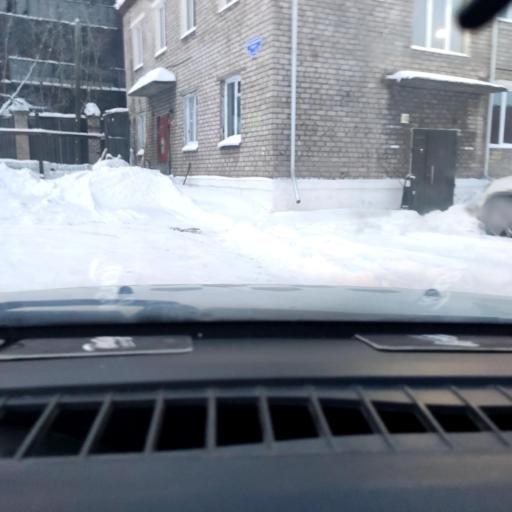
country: RU
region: Perm
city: Perm
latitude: 58.0135
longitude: 56.2015
